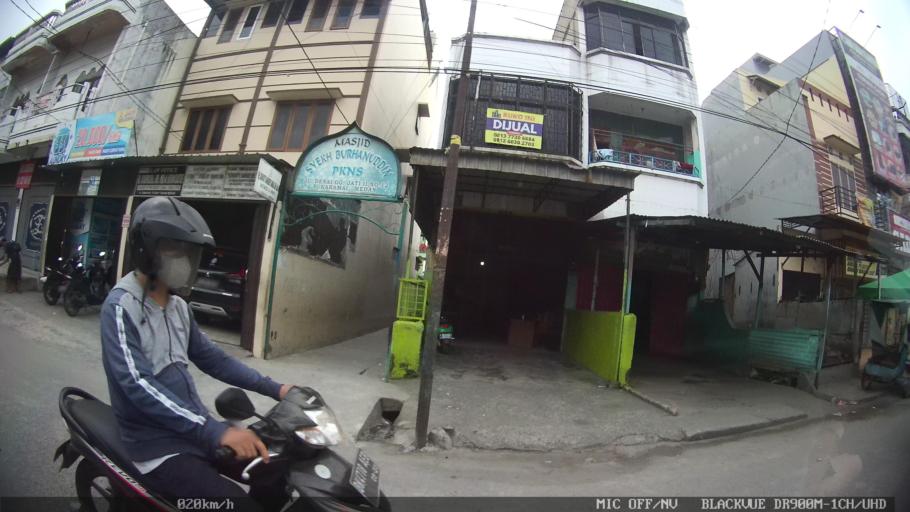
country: ID
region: North Sumatra
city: Medan
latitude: 3.5821
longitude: 98.7050
